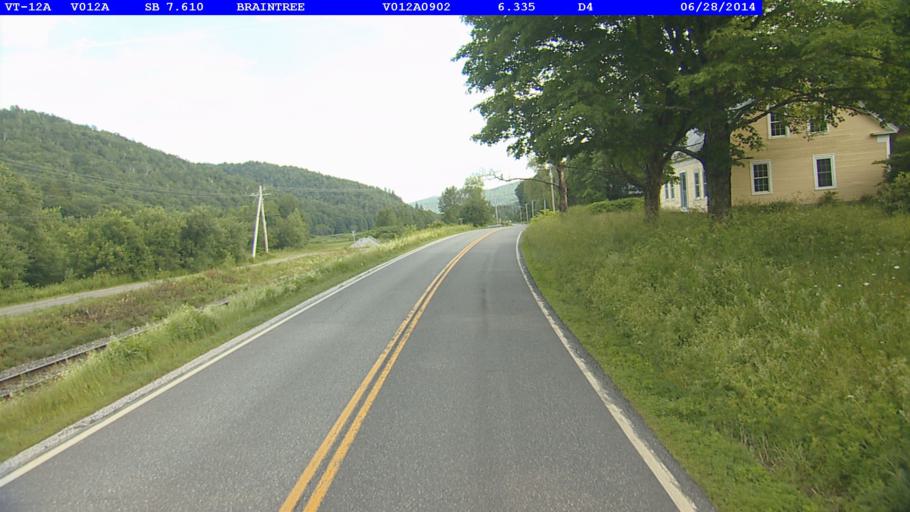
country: US
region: Vermont
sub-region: Orange County
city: Randolph
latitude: 43.9985
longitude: -72.7526
